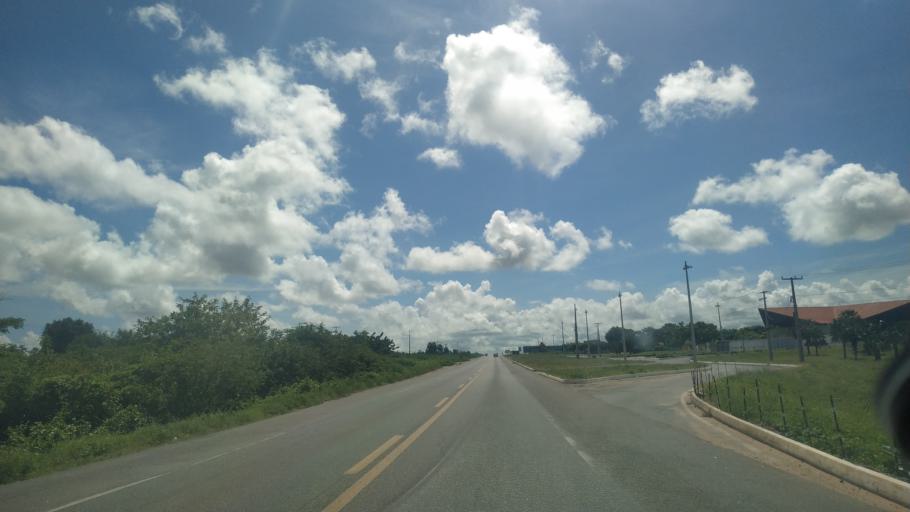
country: BR
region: Rio Grande do Norte
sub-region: Mossoro
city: Mossoro
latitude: -5.1877
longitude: -37.3046
